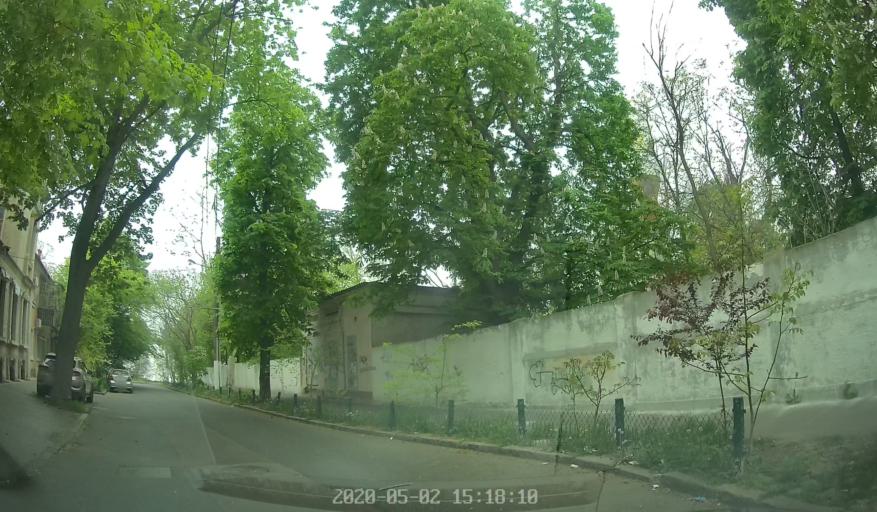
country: TR
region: Kirklareli
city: Sergen
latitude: 41.8248
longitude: 27.6830
